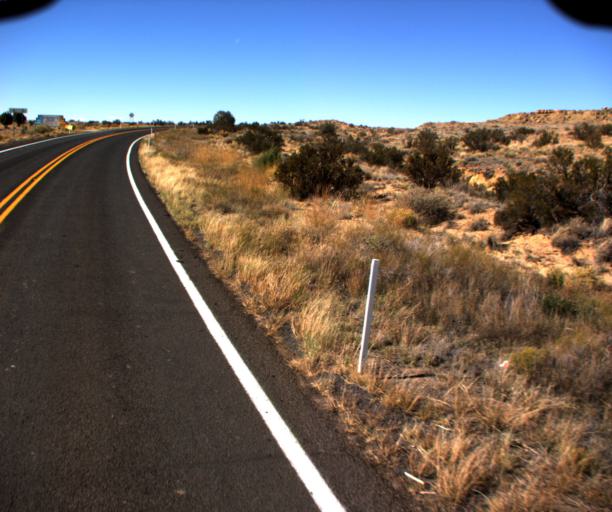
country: US
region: Arizona
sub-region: Navajo County
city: First Mesa
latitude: 35.8808
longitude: -110.6456
